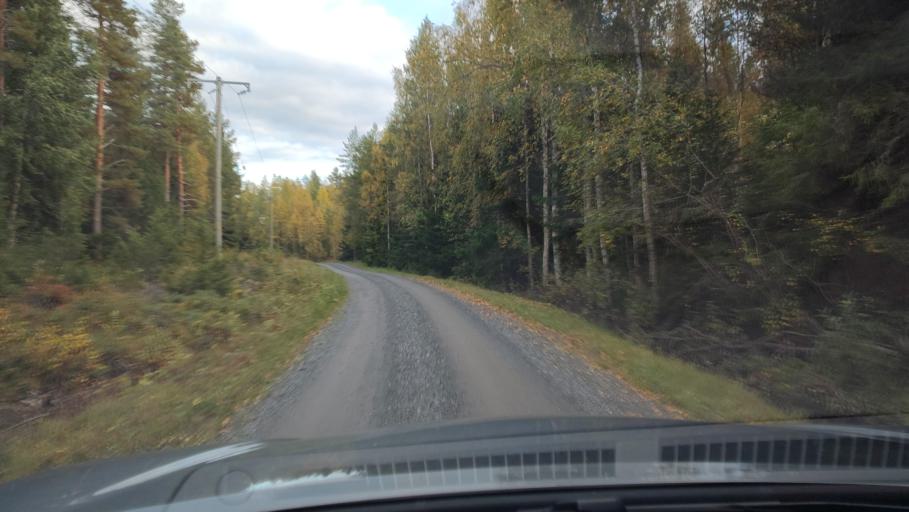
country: FI
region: Ostrobothnia
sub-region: Sydosterbotten
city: Kristinestad
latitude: 62.2324
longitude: 21.4023
